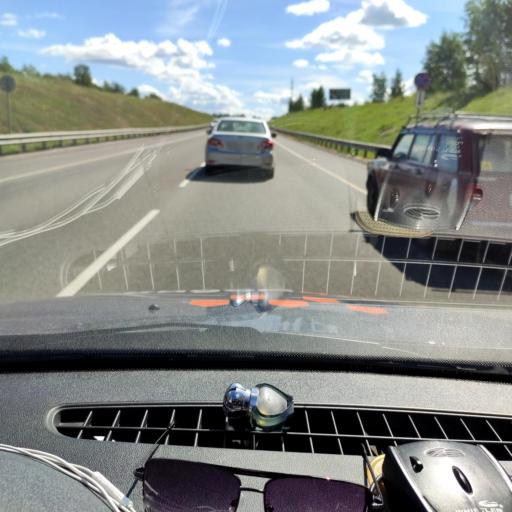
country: RU
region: Lipetsk
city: Borinskoye
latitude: 52.4746
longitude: 39.3983
